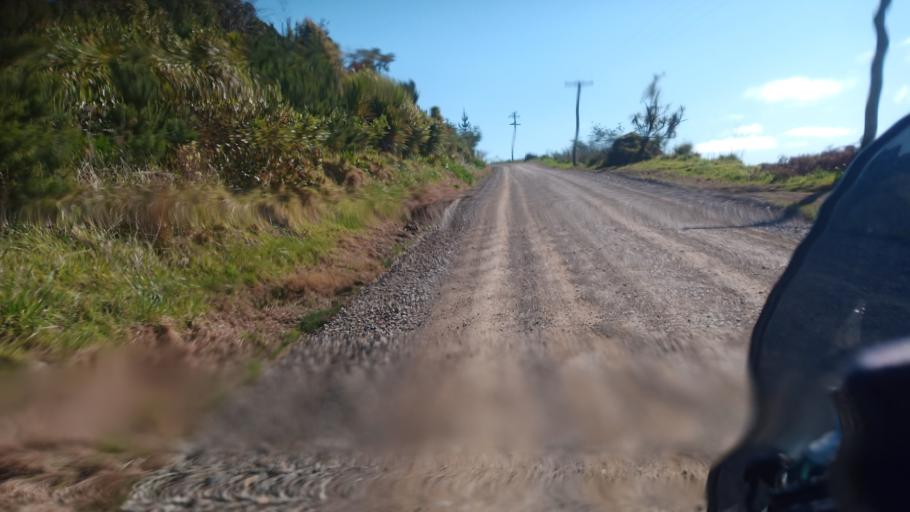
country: NZ
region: Gisborne
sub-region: Gisborne District
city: Gisborne
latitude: -39.1302
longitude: 177.9512
